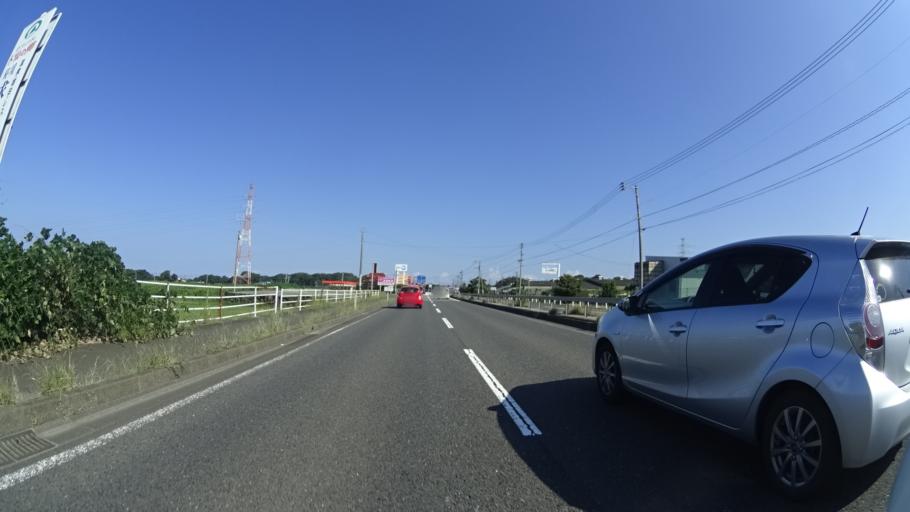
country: JP
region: Fukuoka
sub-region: Buzen-shi
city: Buzen
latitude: 33.6110
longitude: 131.1072
